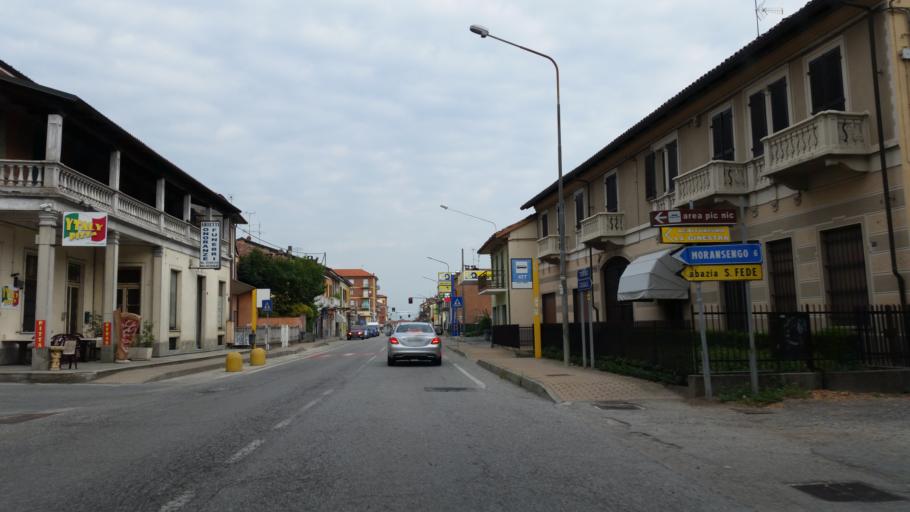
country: IT
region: Piedmont
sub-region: Provincia di Torino
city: Cavagnolo
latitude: 45.1510
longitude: 8.0524
